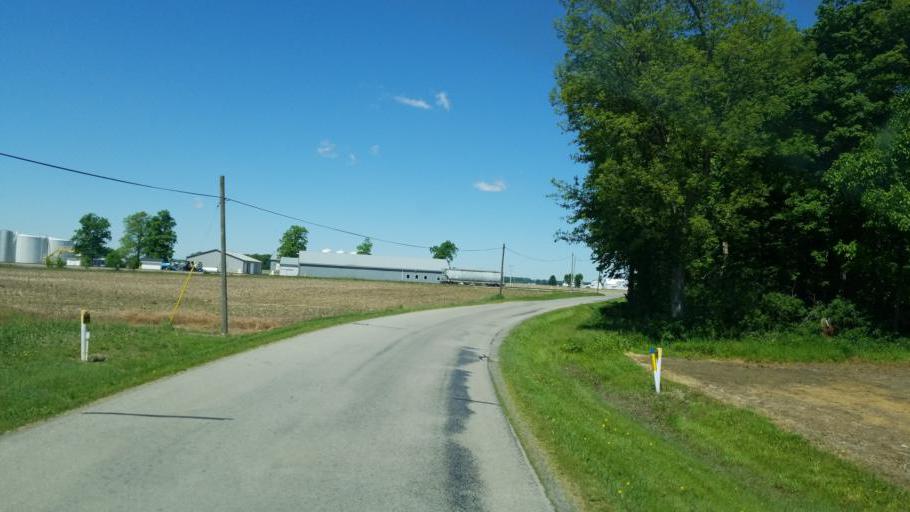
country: US
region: Ohio
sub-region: Shelby County
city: Jackson Center
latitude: 40.4175
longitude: -84.0306
